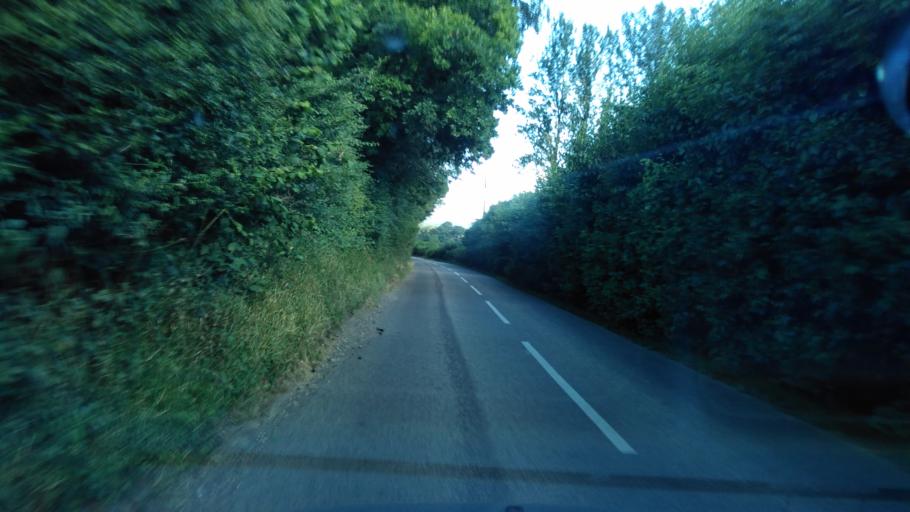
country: GB
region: England
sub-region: Kent
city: Dunkirk
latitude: 51.2504
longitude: 0.9604
